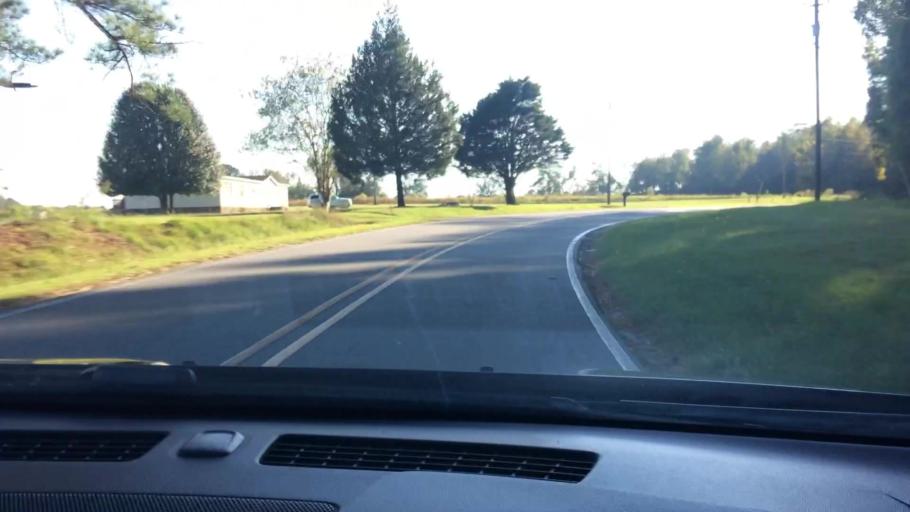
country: US
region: North Carolina
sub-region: Pitt County
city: Winterville
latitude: 35.5133
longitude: -77.4320
